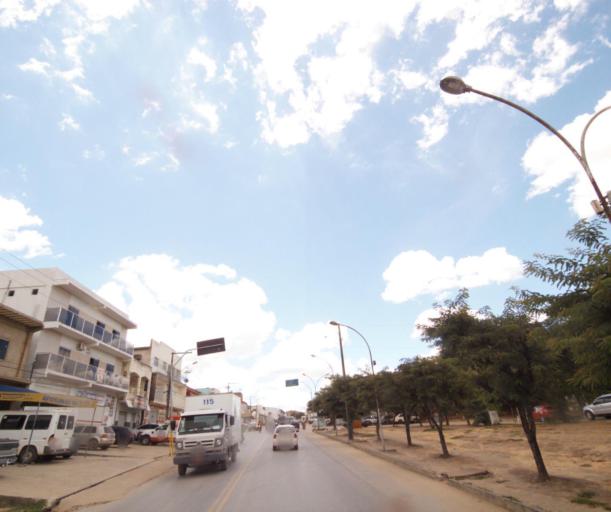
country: BR
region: Bahia
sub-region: Sao Felix Do Coribe
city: Santa Maria da Vitoria
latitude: -13.3984
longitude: -44.2038
